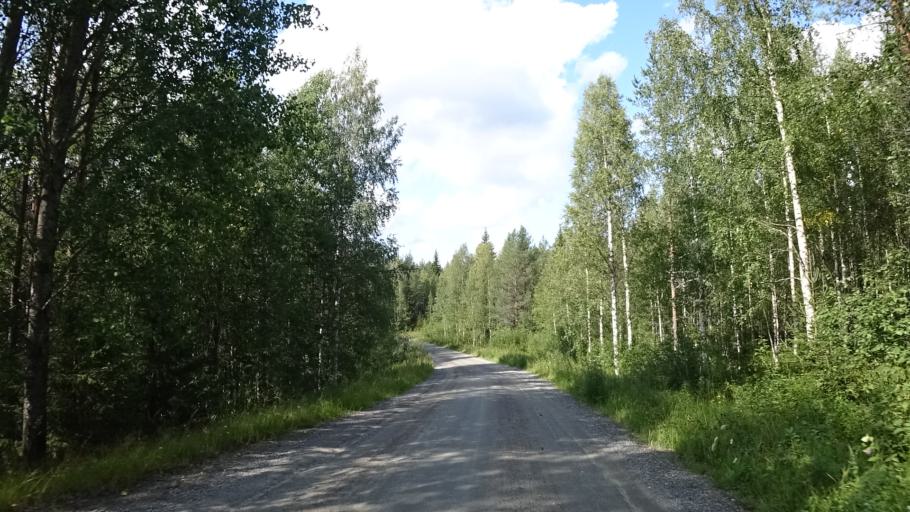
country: FI
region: North Karelia
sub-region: Joensuu
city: Ilomantsi
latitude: 62.9330
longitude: 31.3068
